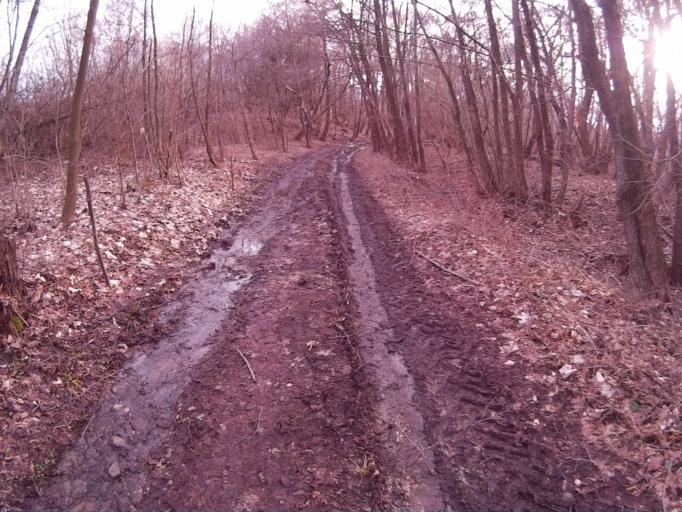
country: HU
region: Borsod-Abauj-Zemplen
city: Gonc
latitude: 48.3989
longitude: 21.3493
